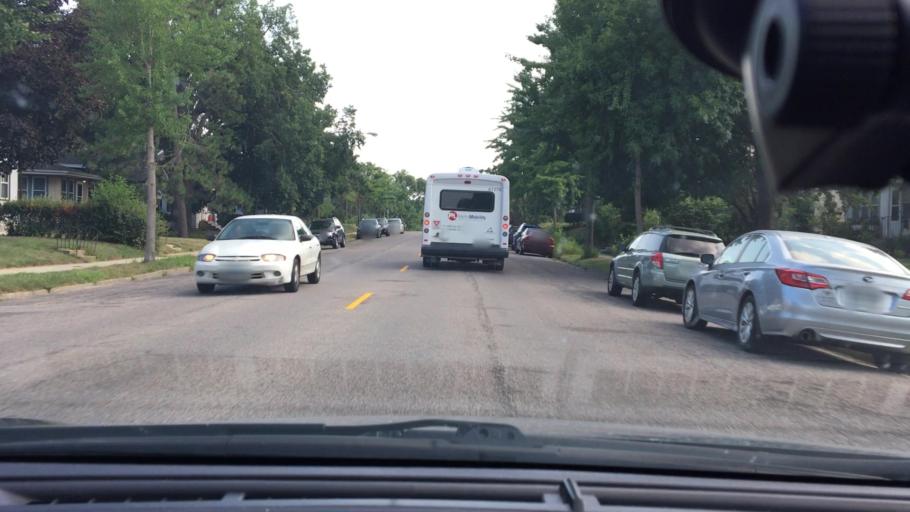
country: US
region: Minnesota
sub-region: Hennepin County
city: Richfield
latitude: 44.9171
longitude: -93.2524
